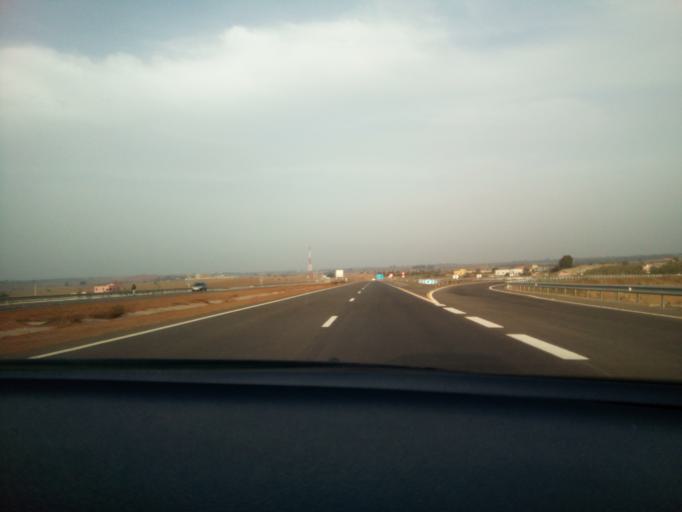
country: MA
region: Rabat-Sale-Zemmour-Zaer
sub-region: Skhirate-Temara
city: Temara
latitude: 33.8459
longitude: -6.8396
